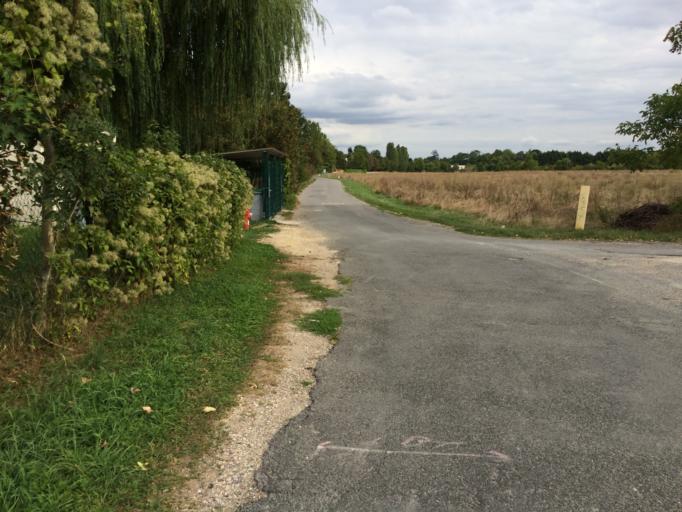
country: FR
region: Ile-de-France
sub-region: Departement de l'Essonne
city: Soisy-sur-Seine
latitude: 48.6531
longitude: 2.4357
